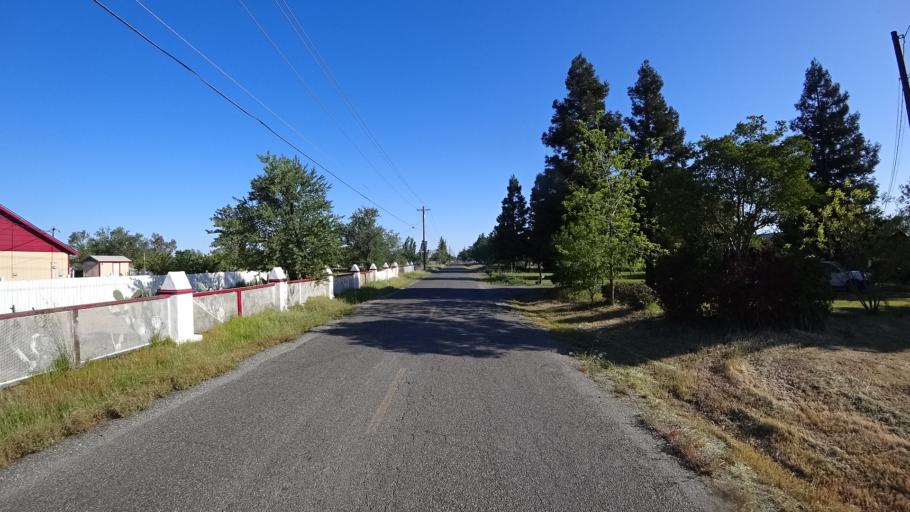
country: US
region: California
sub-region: Glenn County
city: Orland
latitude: 39.7287
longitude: -122.1876
